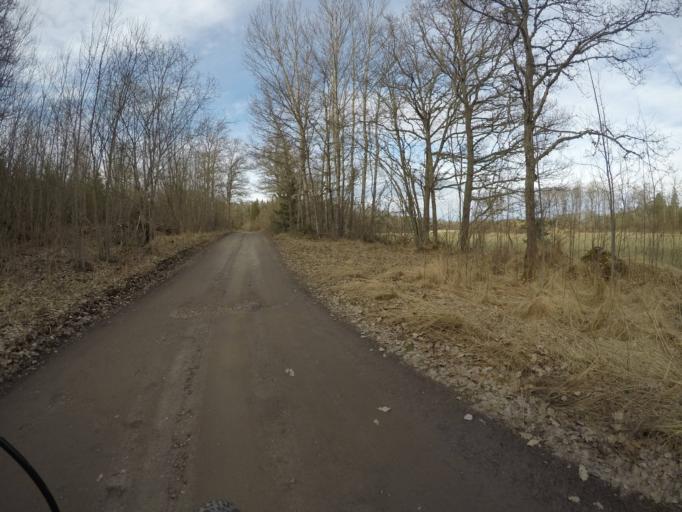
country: SE
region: Soedermanland
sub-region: Eskilstuna Kommun
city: Kvicksund
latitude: 59.4388
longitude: 16.3726
